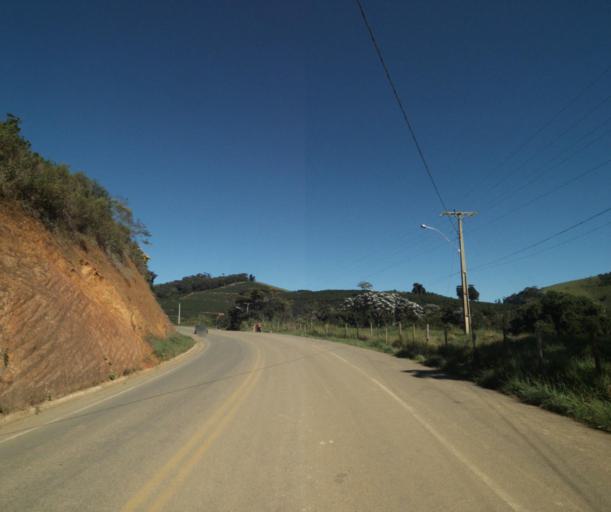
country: BR
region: Minas Gerais
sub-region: Espera Feliz
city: Espera Feliz
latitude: -20.6865
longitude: -41.8445
